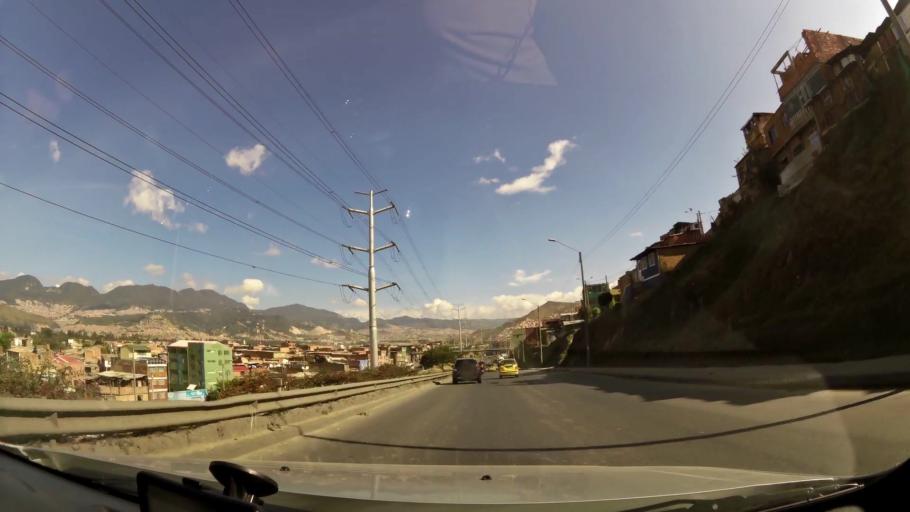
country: CO
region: Bogota D.C.
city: Bogota
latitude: 4.5574
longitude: -74.1387
